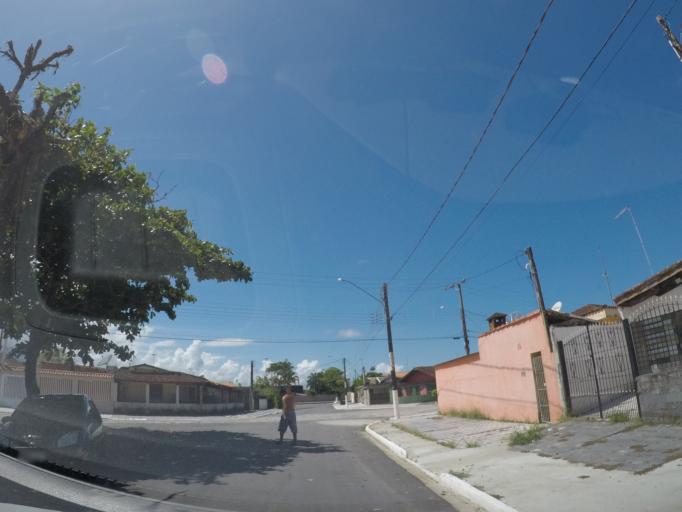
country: BR
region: Sao Paulo
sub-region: Mongagua
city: Mongagua
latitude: -24.0625
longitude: -46.5589
